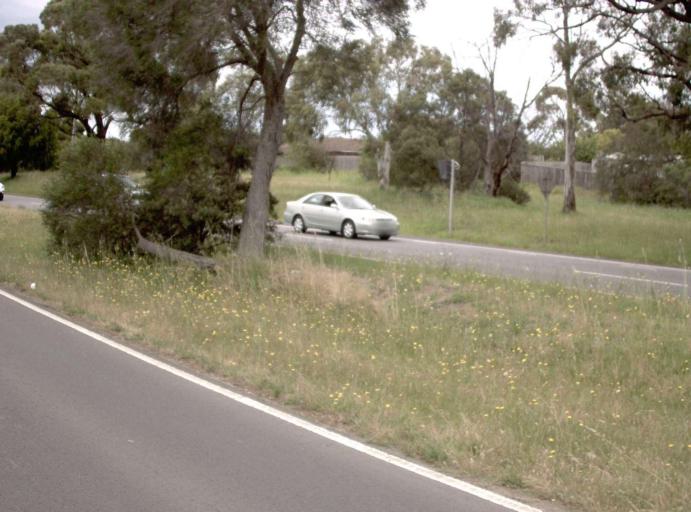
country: AU
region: Victoria
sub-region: Casey
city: Cranbourne North
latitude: -38.0772
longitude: 145.2734
